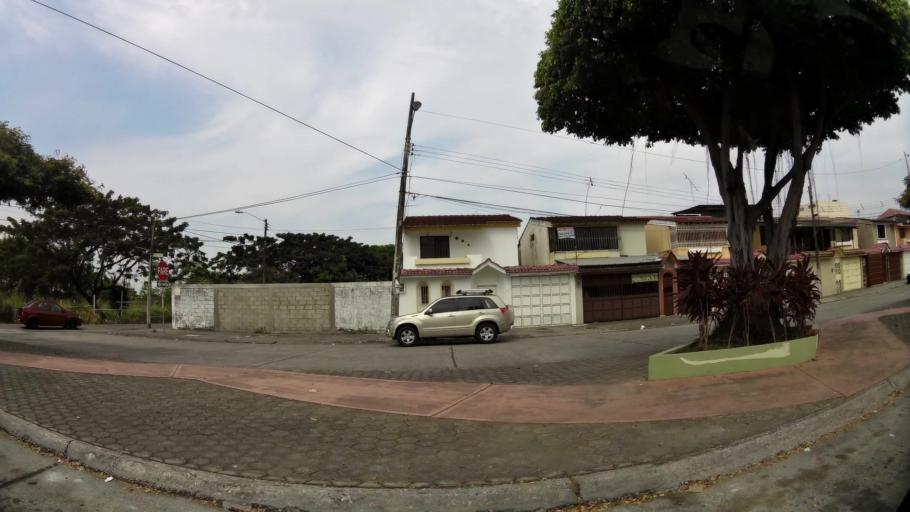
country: EC
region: Guayas
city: Eloy Alfaro
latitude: -2.1160
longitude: -79.8884
